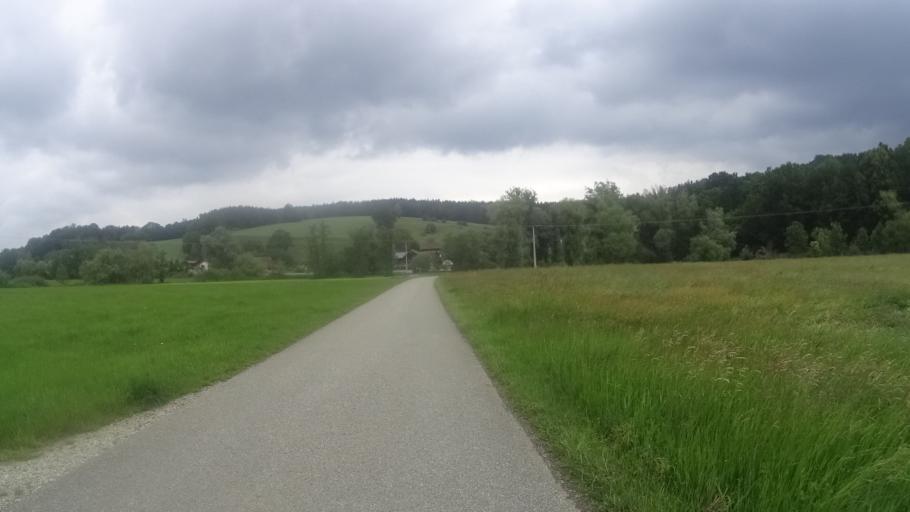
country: DE
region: Bavaria
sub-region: Lower Bavaria
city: Triftern
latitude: 48.4358
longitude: 12.9968
